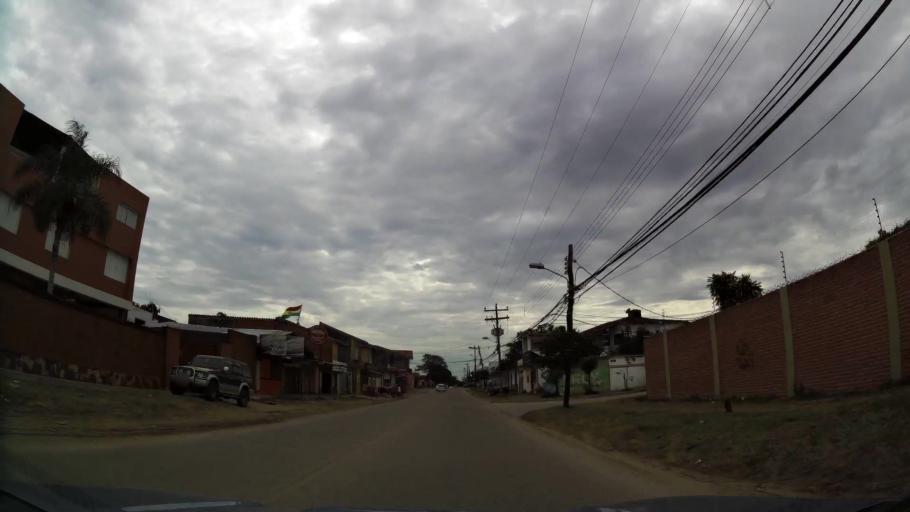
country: BO
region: Santa Cruz
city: Santa Cruz de la Sierra
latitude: -17.7473
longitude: -63.1797
